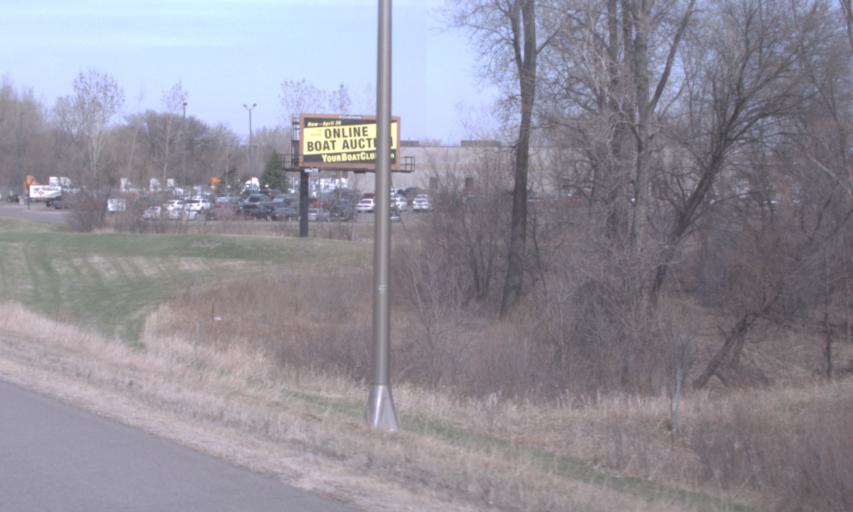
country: US
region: Minnesota
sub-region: Anoka County
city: Coon Rapids
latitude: 45.1720
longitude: -93.2972
